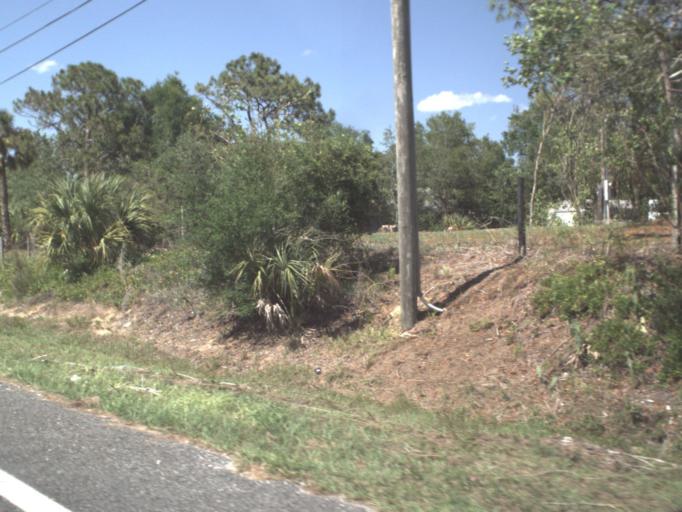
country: US
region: Florida
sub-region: Brevard County
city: Mims
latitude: 28.7631
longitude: -80.8764
